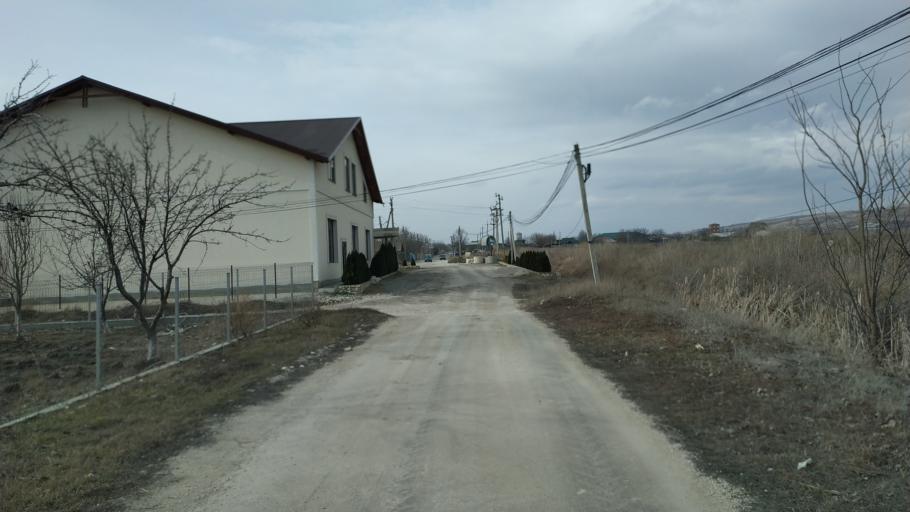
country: MD
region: Laloveni
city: Ialoveni
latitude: 46.8582
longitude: 28.7890
